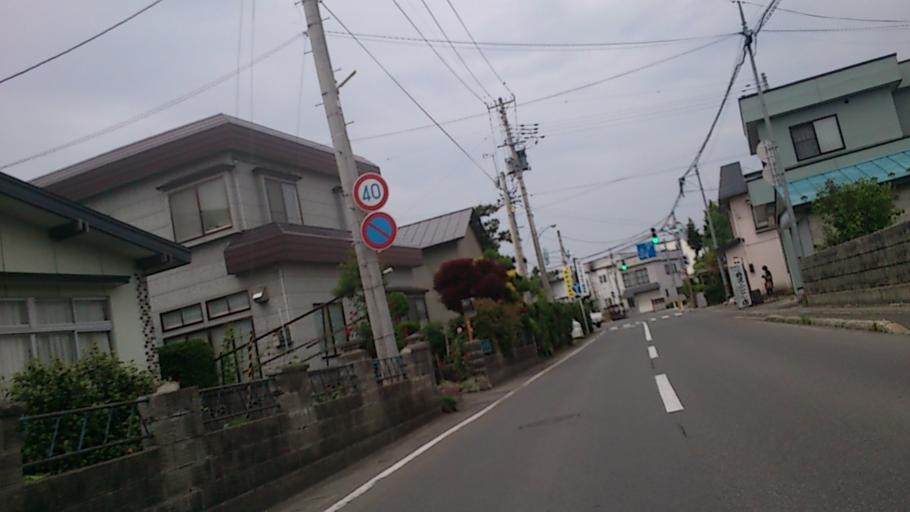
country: JP
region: Aomori
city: Hirosaki
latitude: 40.5927
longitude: 140.4284
